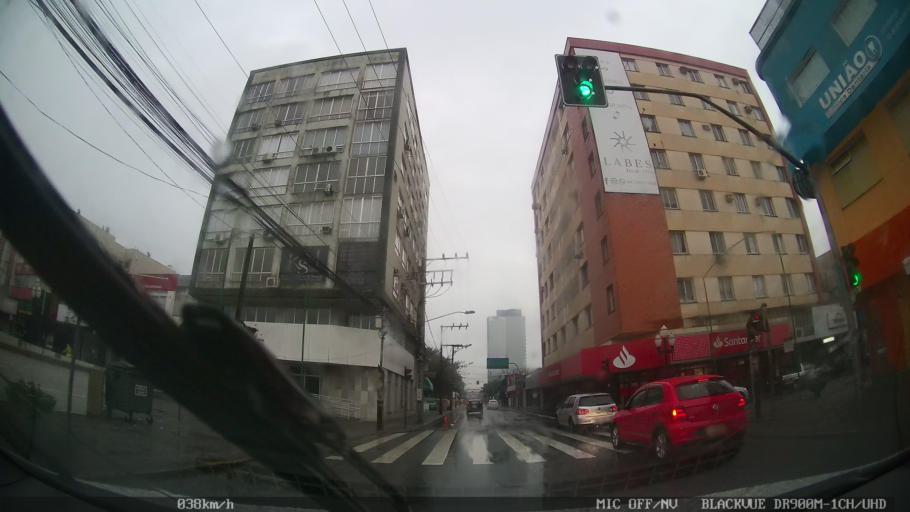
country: BR
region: Santa Catarina
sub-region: Itajai
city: Itajai
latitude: -26.9064
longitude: -48.6595
